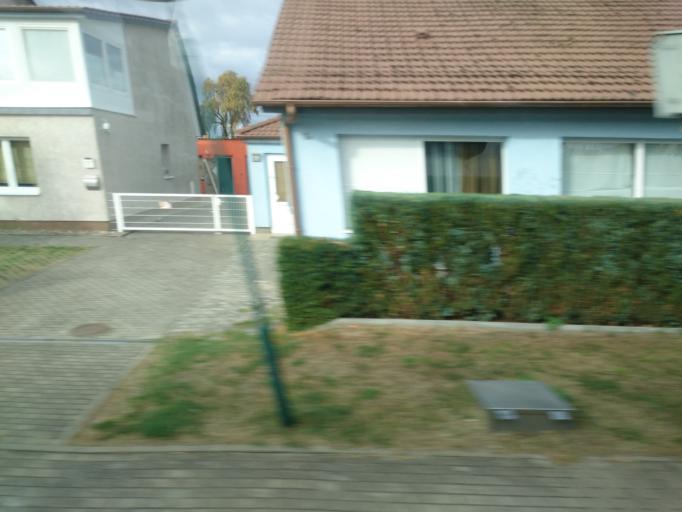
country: DE
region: Mecklenburg-Vorpommern
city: Pasewalk
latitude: 53.5188
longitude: 13.9775
